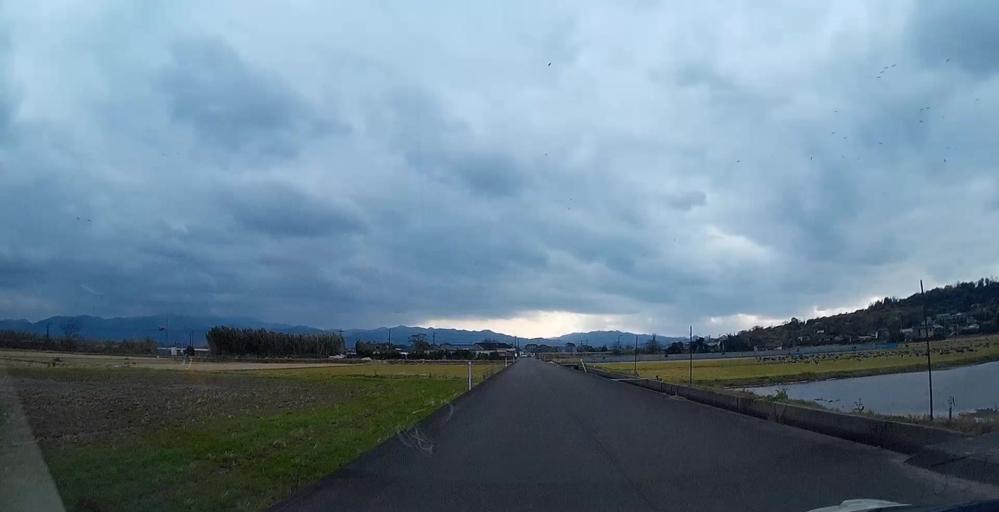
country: JP
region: Kagoshima
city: Izumi
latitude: 32.0982
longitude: 130.2754
